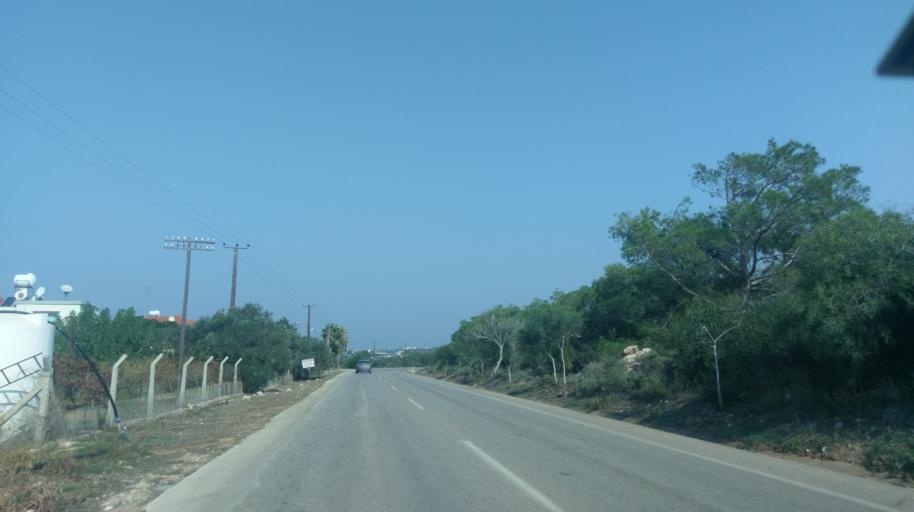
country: CY
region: Ammochostos
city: Leonarisso
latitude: 35.4877
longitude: 34.1521
